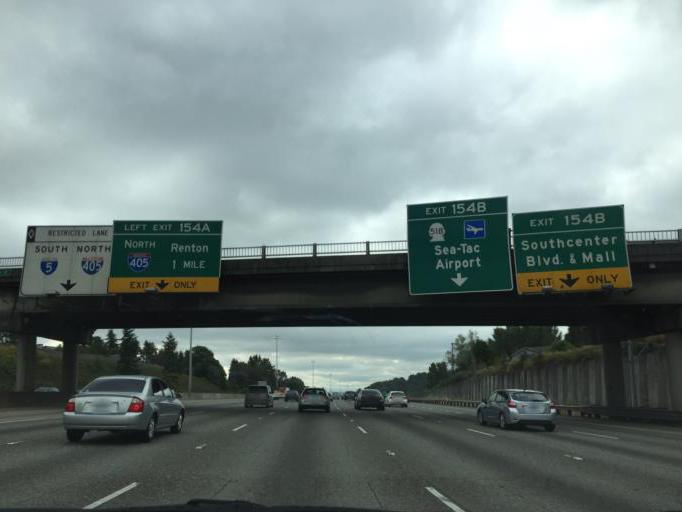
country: US
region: Washington
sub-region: King County
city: Tukwila
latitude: 47.4742
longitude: -122.2699
